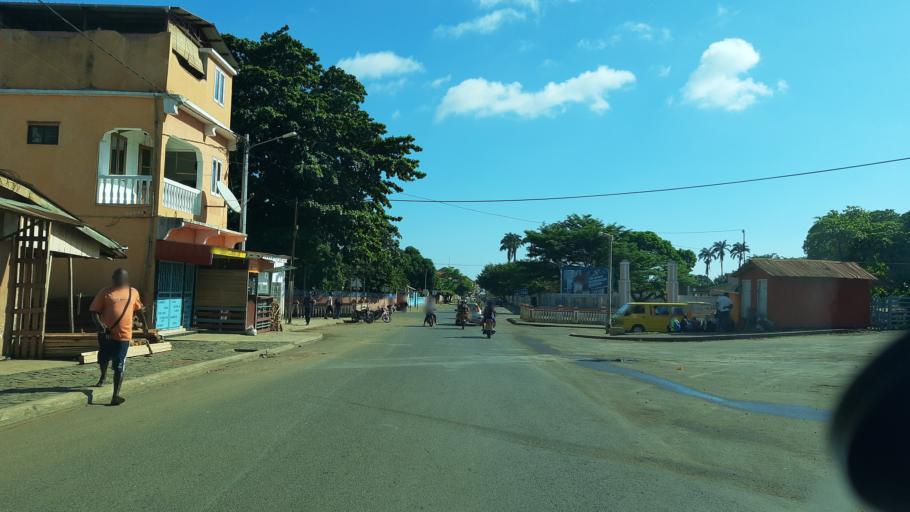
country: ST
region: Sao Tome Island
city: Sao Tome
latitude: 0.3337
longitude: 6.7304
